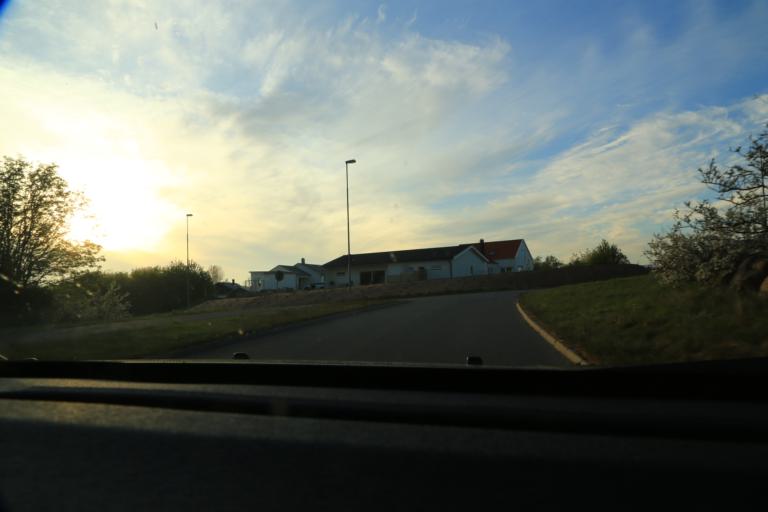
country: SE
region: Halland
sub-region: Varbergs Kommun
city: Traslovslage
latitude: 57.0626
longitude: 12.2903
